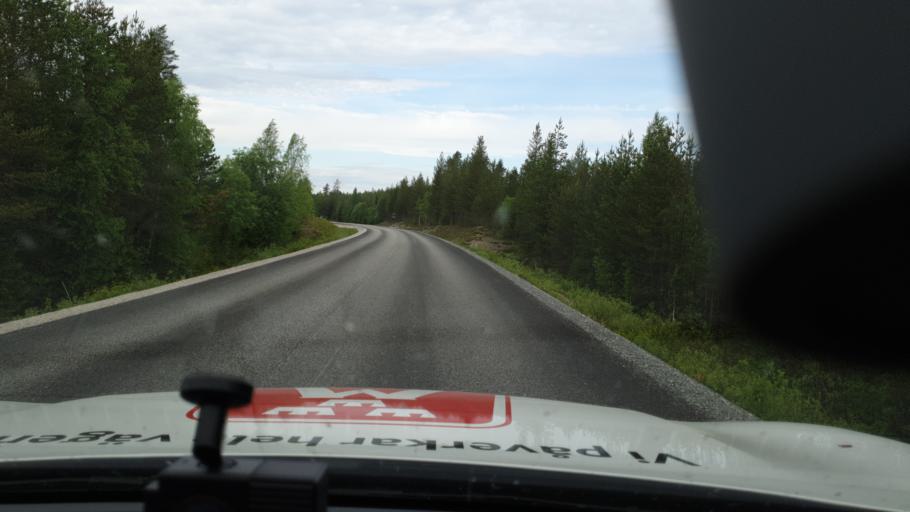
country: SE
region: Vaesterbotten
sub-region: Mala Kommun
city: Mala
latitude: 64.9821
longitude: 18.5560
